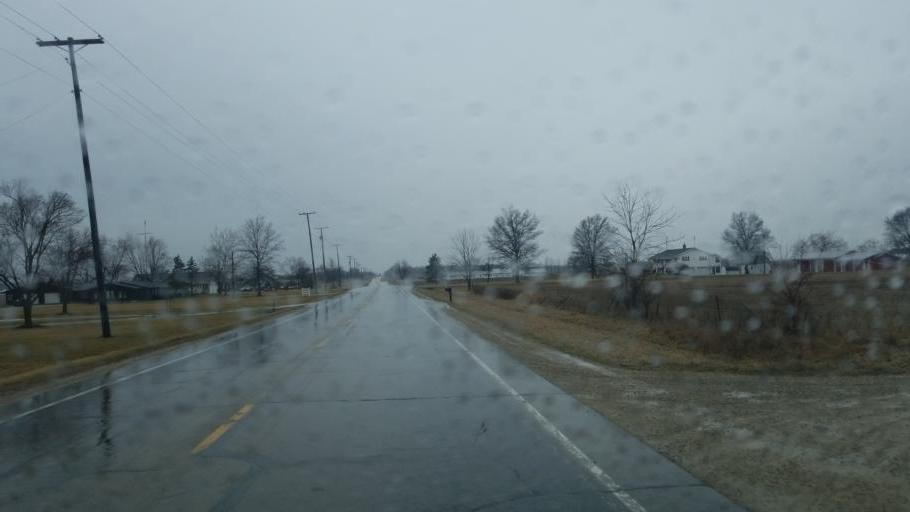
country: US
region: Indiana
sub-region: Adams County
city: Berne
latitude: 40.6566
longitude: -85.0021
